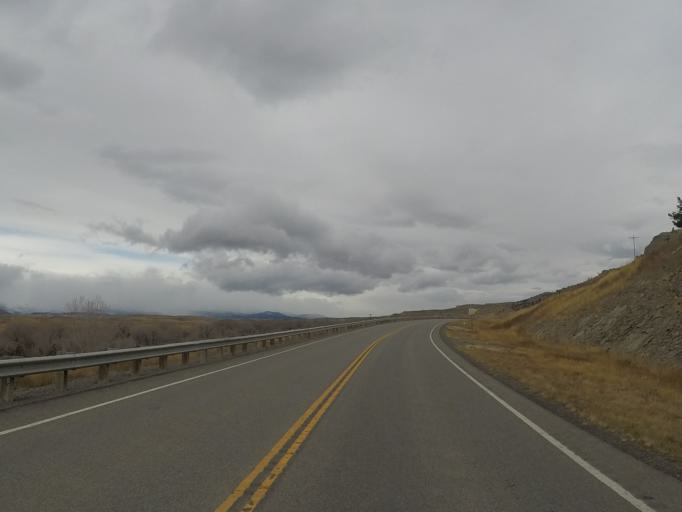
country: US
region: Montana
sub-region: Sweet Grass County
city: Big Timber
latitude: 45.8815
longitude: -109.9561
